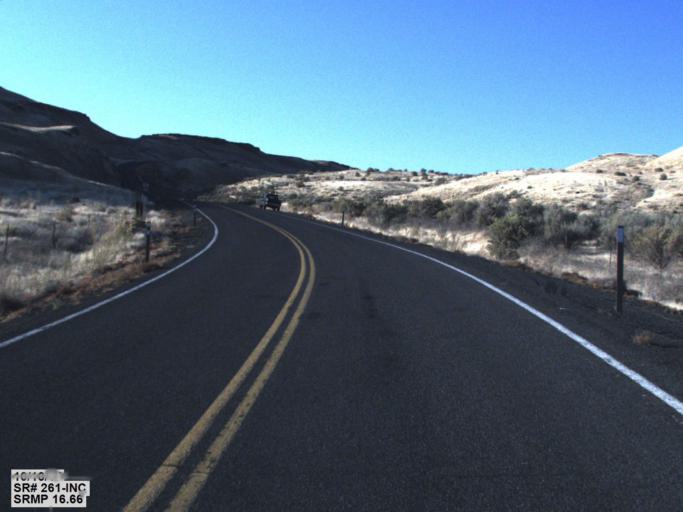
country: US
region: Washington
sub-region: Walla Walla County
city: Waitsburg
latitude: 46.6106
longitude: -118.2229
